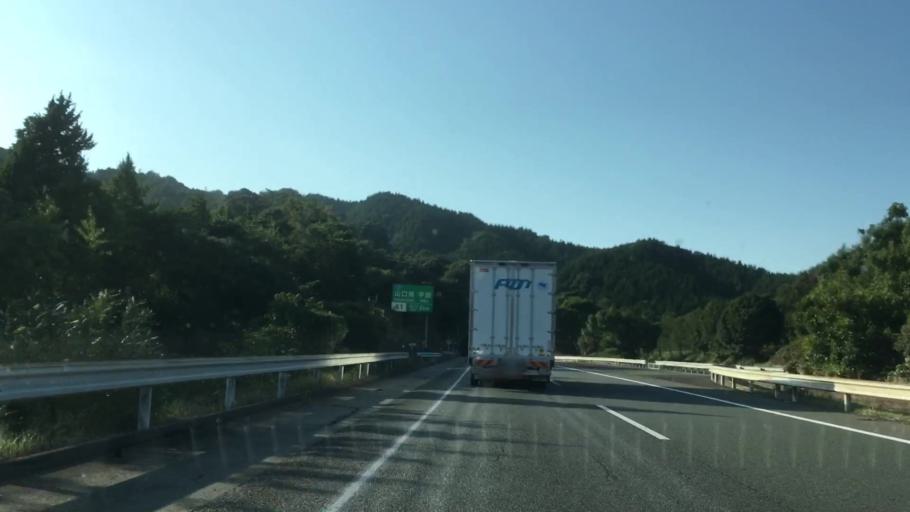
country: JP
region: Yamaguchi
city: Hofu
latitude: 34.0775
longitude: 131.4892
